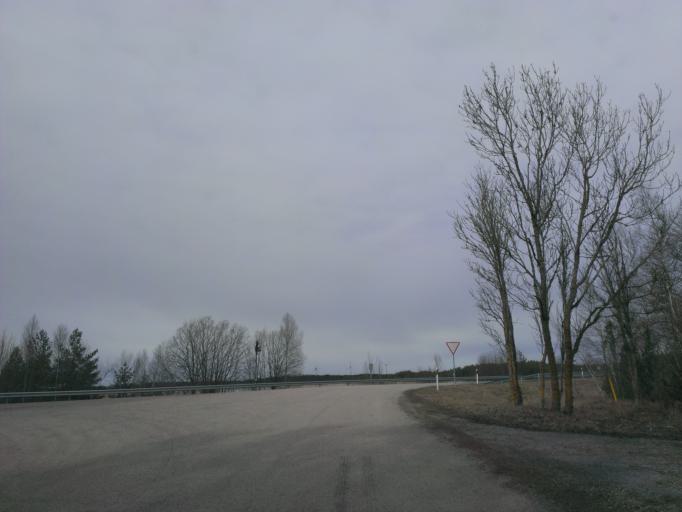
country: EE
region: Laeaene
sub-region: Lihula vald
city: Lihula
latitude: 58.5898
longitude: 23.5374
